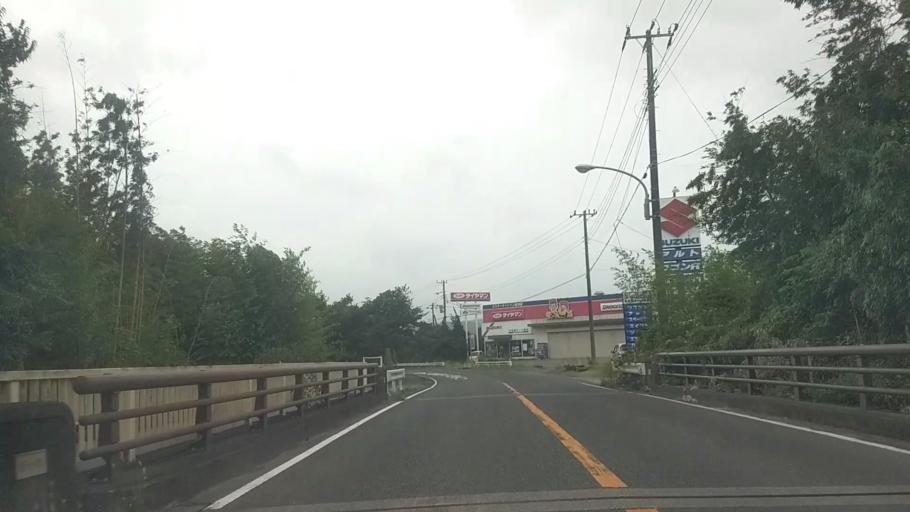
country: JP
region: Chiba
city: Kimitsu
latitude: 35.2175
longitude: 139.8913
